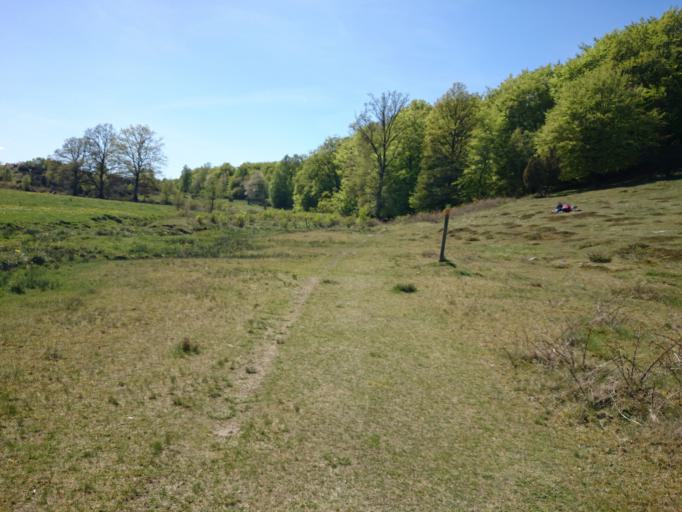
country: SE
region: Skane
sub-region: Lunds Kommun
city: Genarp
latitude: 55.6629
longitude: 13.4062
